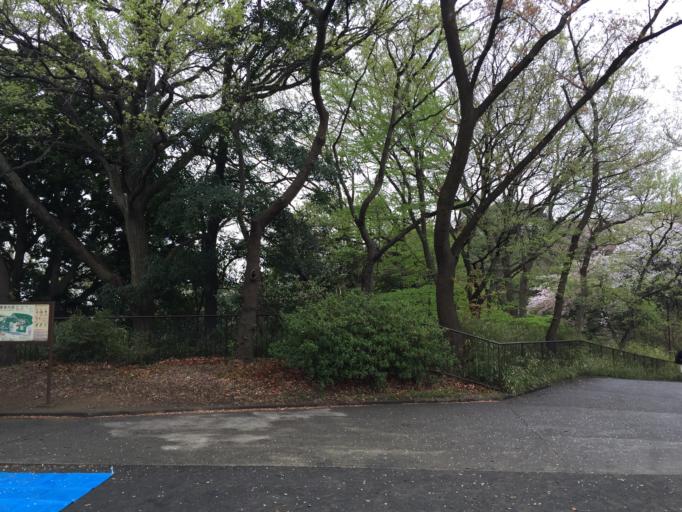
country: JP
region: Kanagawa
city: Yokohama
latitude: 35.4245
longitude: 139.5956
